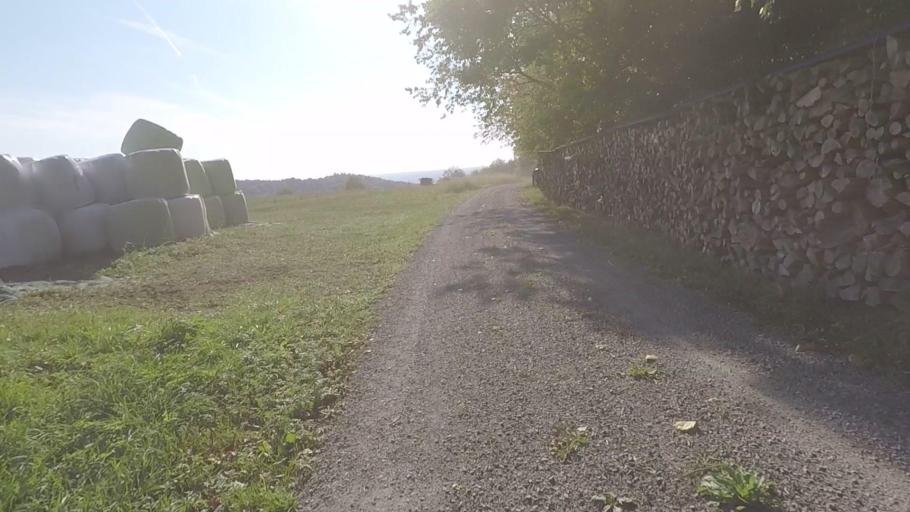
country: DE
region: Baden-Wuerttemberg
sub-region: Regierungsbezirk Stuttgart
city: Spiegelberg
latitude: 49.0476
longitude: 9.4622
